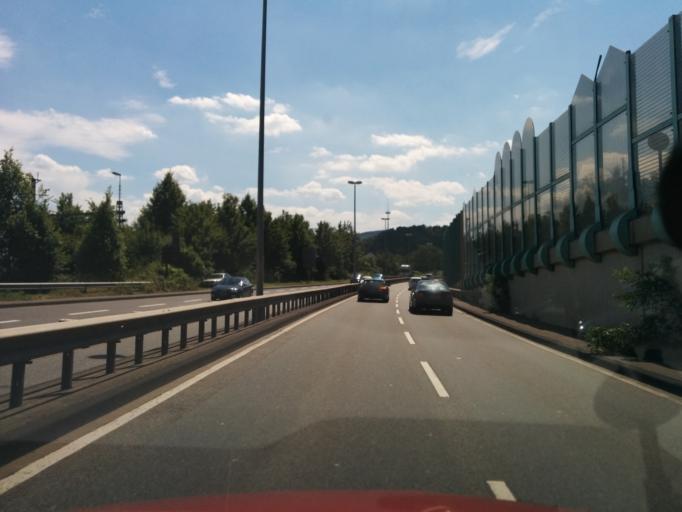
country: DE
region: Rheinland-Pfalz
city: Koblenz
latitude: 50.3470
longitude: 7.5859
